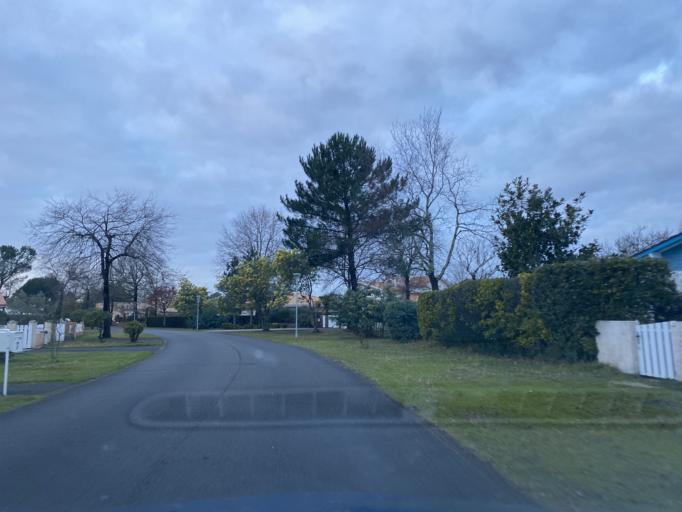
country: FR
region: Aquitaine
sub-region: Departement de la Gironde
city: Andernos-les-Bains
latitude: 44.7517
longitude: -1.0823
